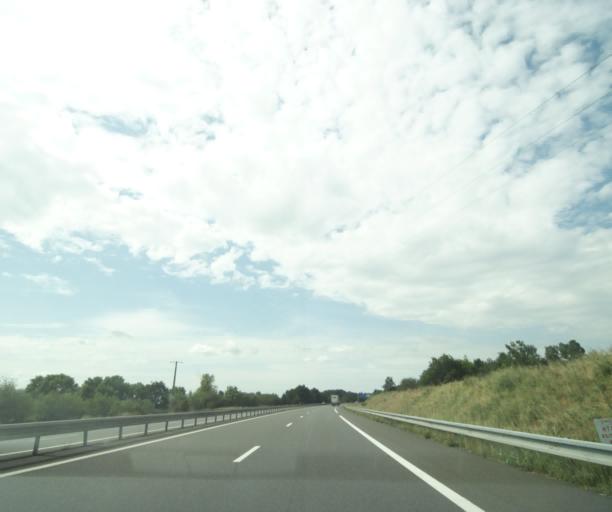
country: FR
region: Pays de la Loire
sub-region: Departement de Maine-et-Loire
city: Jumelles
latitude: 47.3984
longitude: -0.1161
